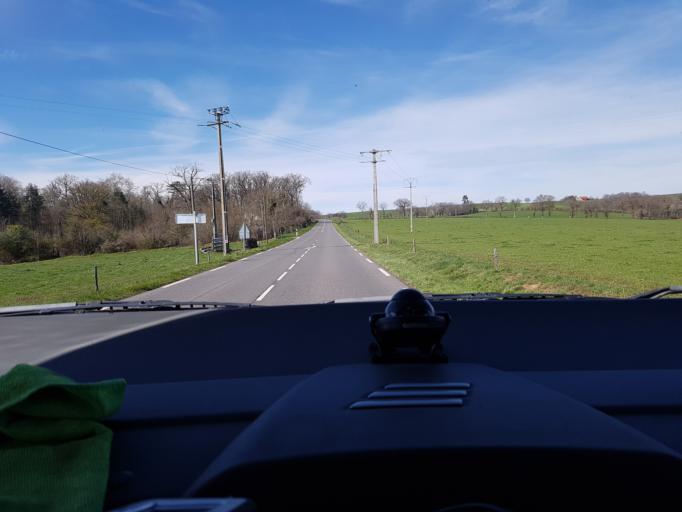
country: FR
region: Auvergne
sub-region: Departement de l'Allier
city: Le Donjon
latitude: 46.2997
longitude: 3.7671
